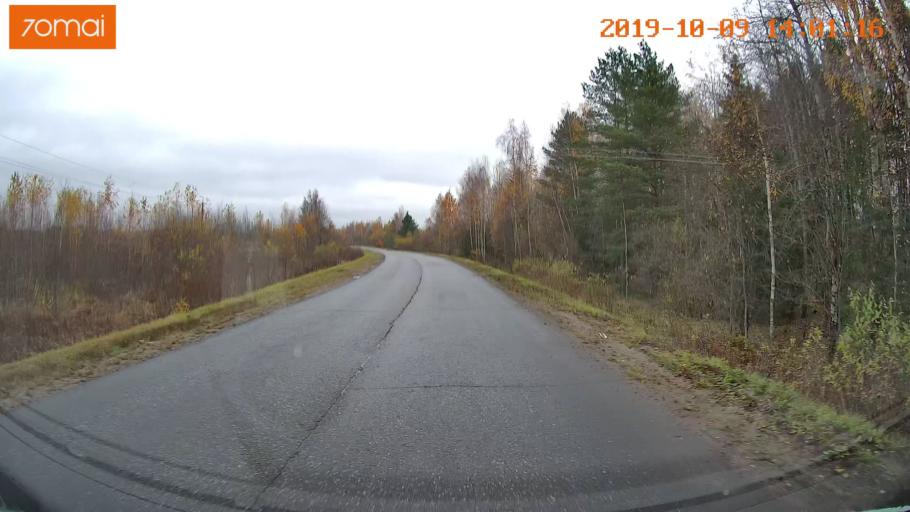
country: RU
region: Kostroma
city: Buy
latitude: 58.4424
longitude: 41.3456
